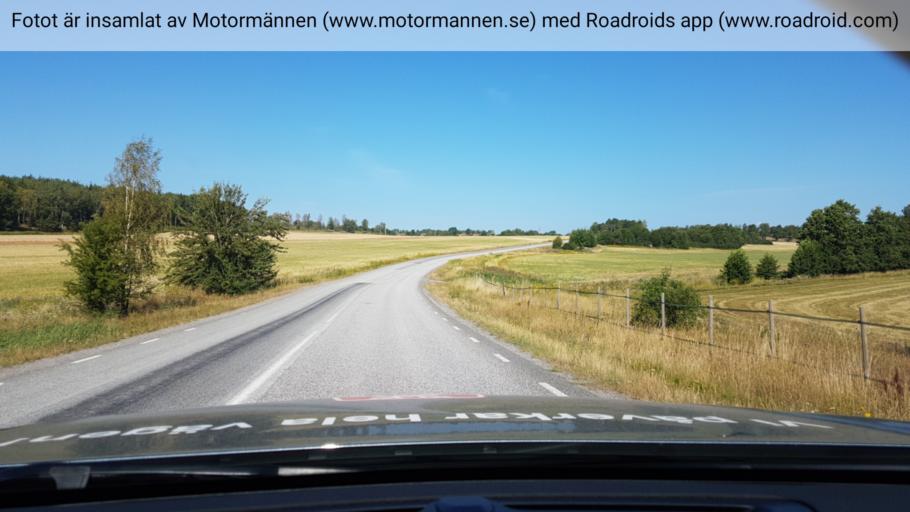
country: SE
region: Stockholm
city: Stenhamra
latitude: 59.3903
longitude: 17.5741
